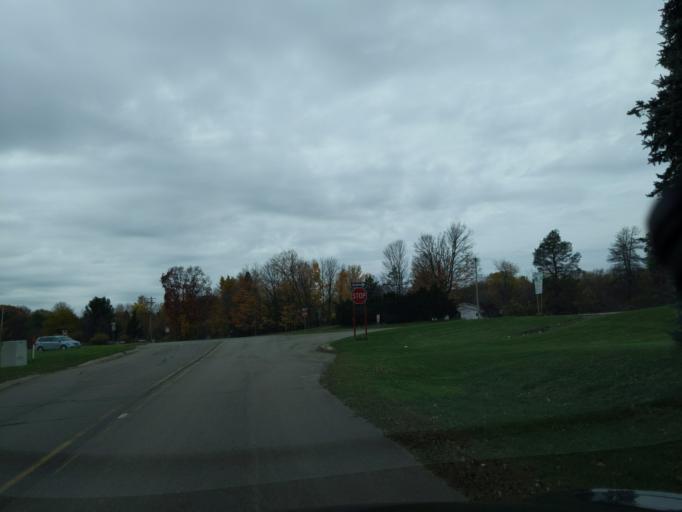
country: US
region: Michigan
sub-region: Eaton County
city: Eaton Rapids
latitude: 42.5530
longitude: -84.6236
